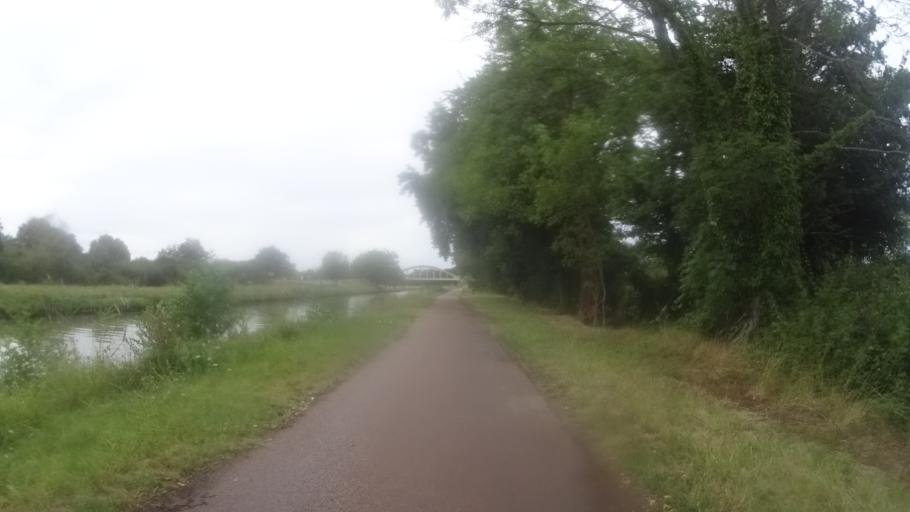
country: FR
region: Bourgogne
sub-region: Departement de la Nievre
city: Saint-Leger-des-Vignes
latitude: 46.8181
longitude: 3.3591
